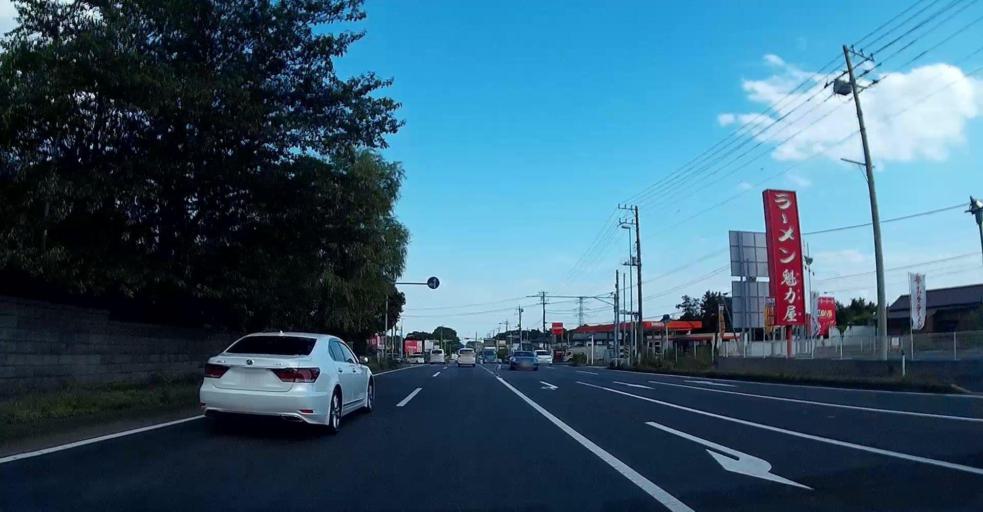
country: JP
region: Chiba
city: Shiroi
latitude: 35.8084
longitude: 140.0386
